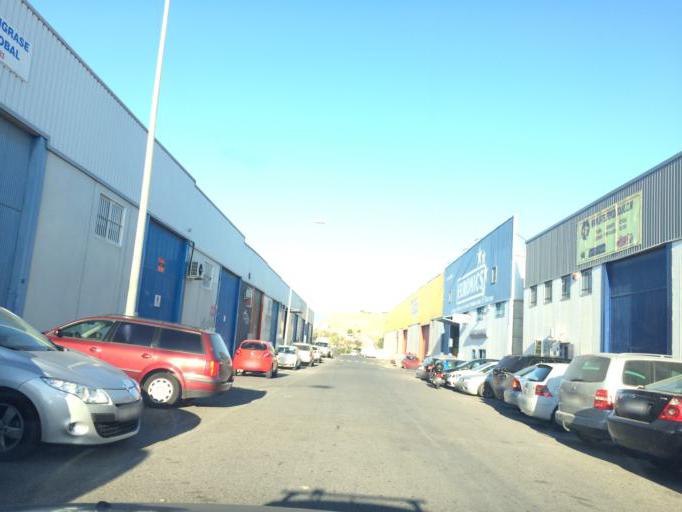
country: ES
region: Andalusia
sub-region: Provincia de Almeria
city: Viator
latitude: 36.8843
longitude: -2.4170
